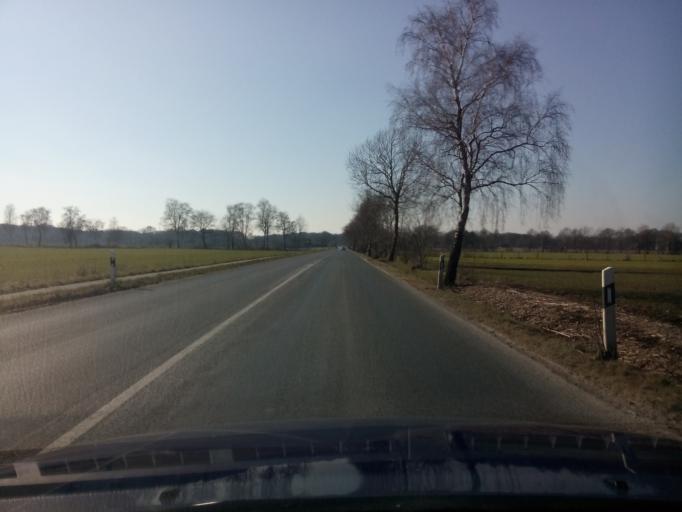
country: DE
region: Lower Saxony
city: Ritterhude
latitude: 53.2302
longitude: 8.6821
